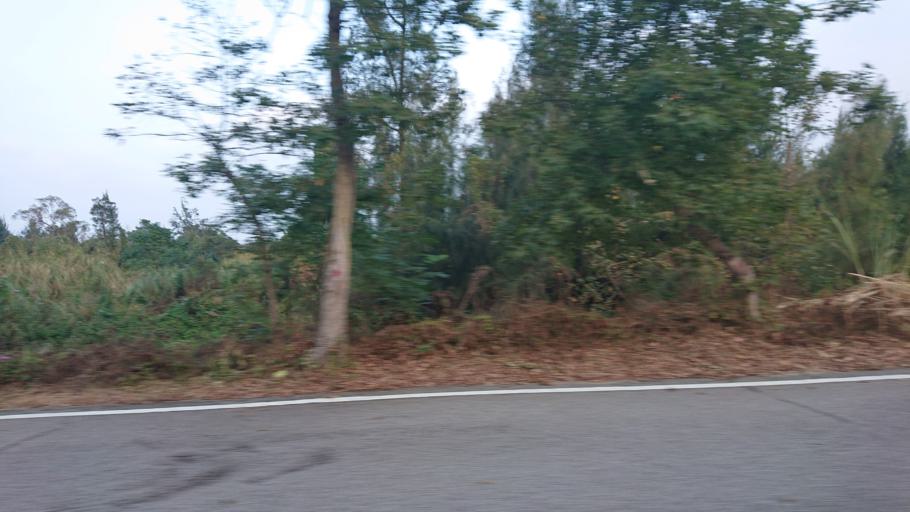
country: CN
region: Fujian
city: Shijing
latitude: 24.4965
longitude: 118.4439
